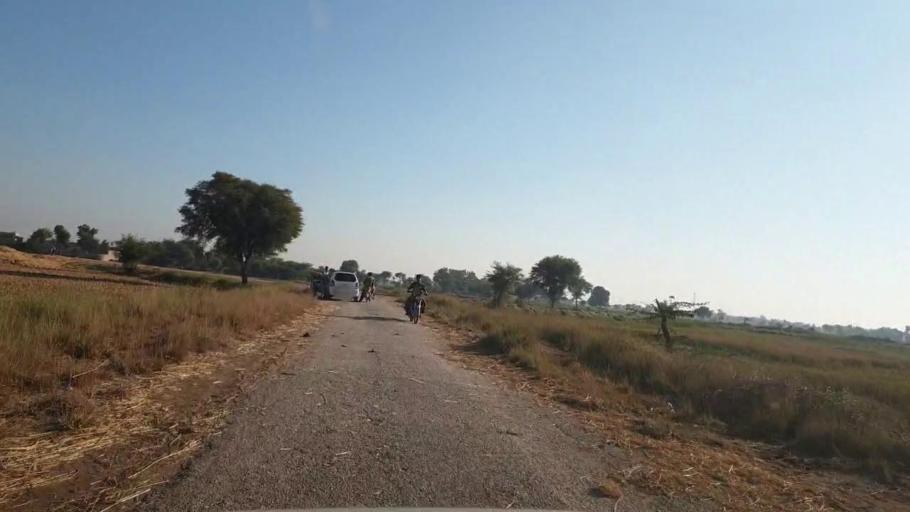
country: PK
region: Sindh
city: Phulji
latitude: 26.9848
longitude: 67.6910
